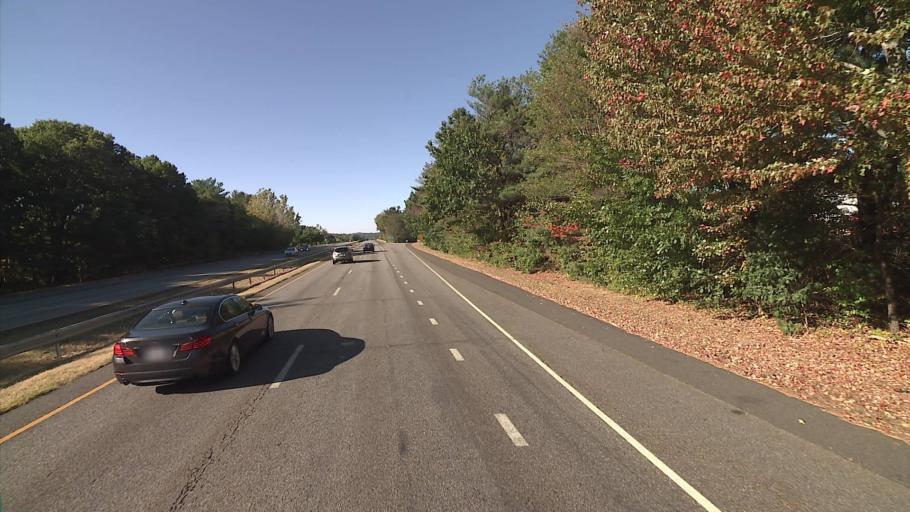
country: US
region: Connecticut
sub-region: New Haven County
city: Wallingford
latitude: 41.4942
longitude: -72.8059
